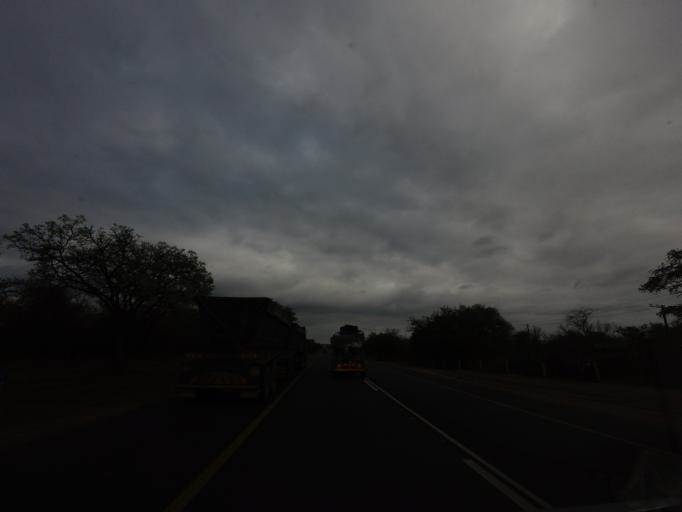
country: ZA
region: Mpumalanga
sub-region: Ehlanzeni District
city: Komatipoort
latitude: -25.4409
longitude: 31.7238
